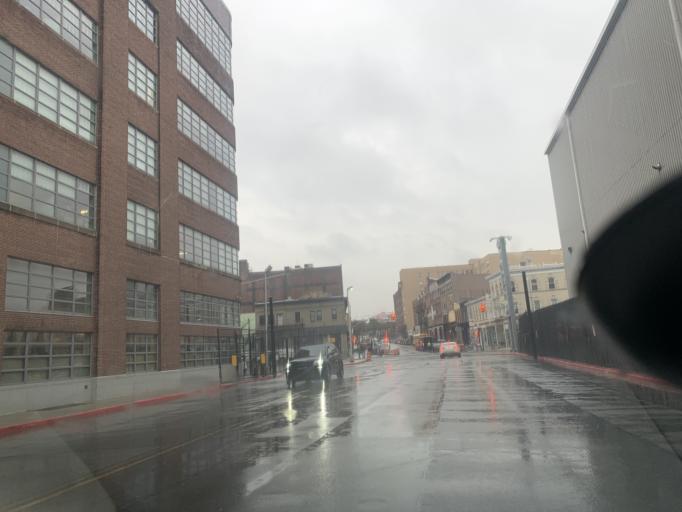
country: US
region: New York
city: New York City
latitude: 40.6984
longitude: -73.9677
